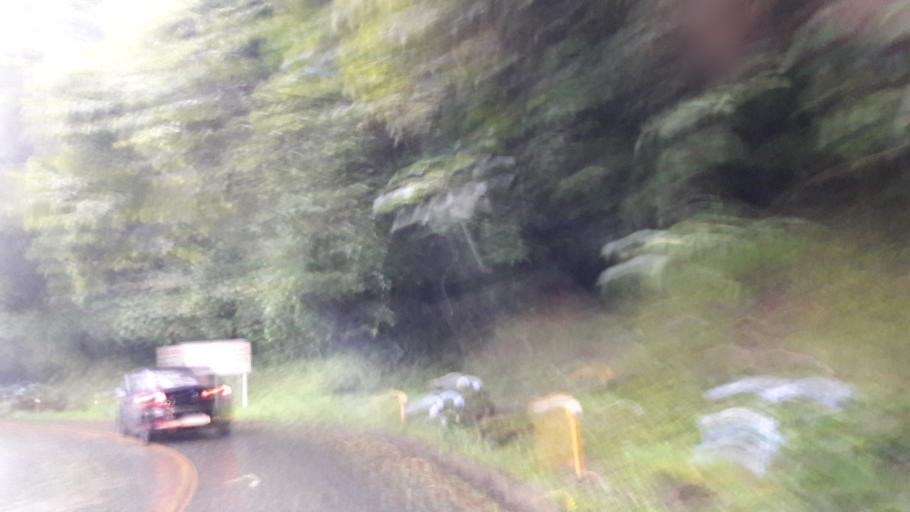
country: BR
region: Parana
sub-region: Campina Grande Do Sul
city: Campina Grande do Sul
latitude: -25.3486
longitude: -48.8861
